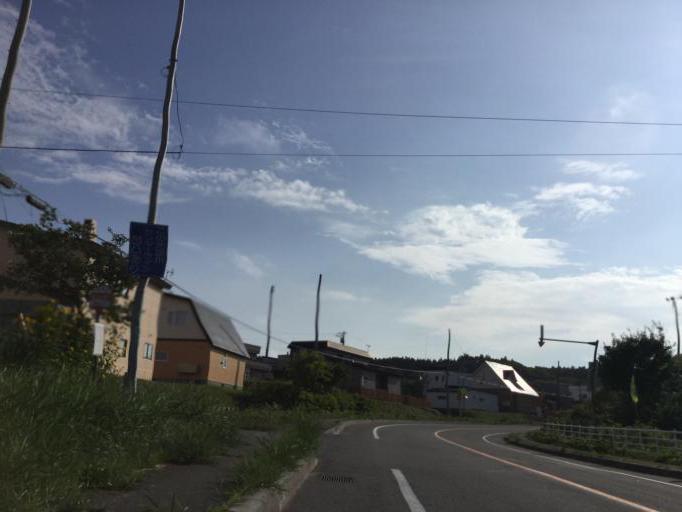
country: JP
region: Hokkaido
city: Wakkanai
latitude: 45.3833
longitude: 141.6660
